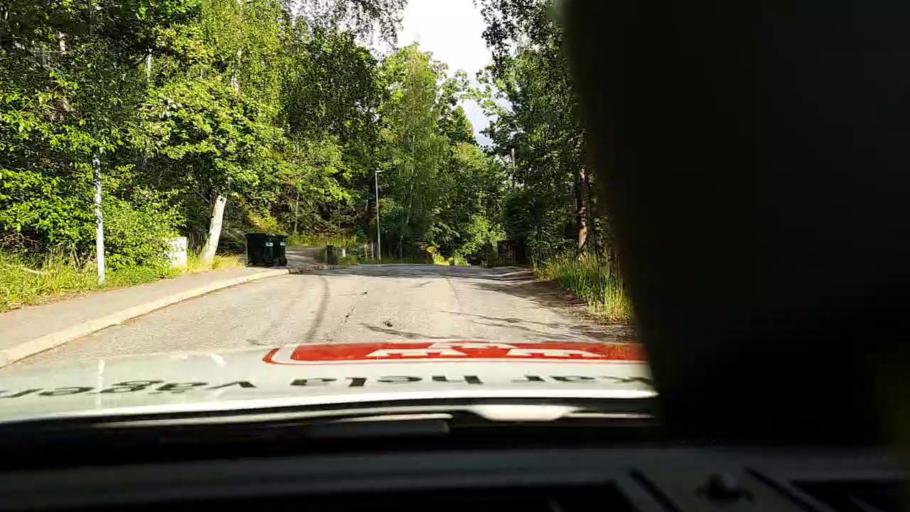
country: SE
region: Stockholm
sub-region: Huddinge Kommun
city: Huddinge
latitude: 59.2617
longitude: 17.9869
